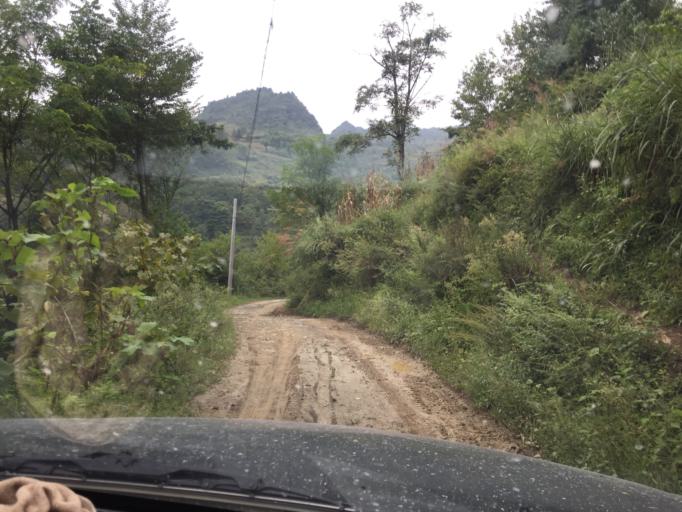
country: CN
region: Guizhou Sheng
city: Nangan
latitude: 28.2521
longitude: 107.9467
